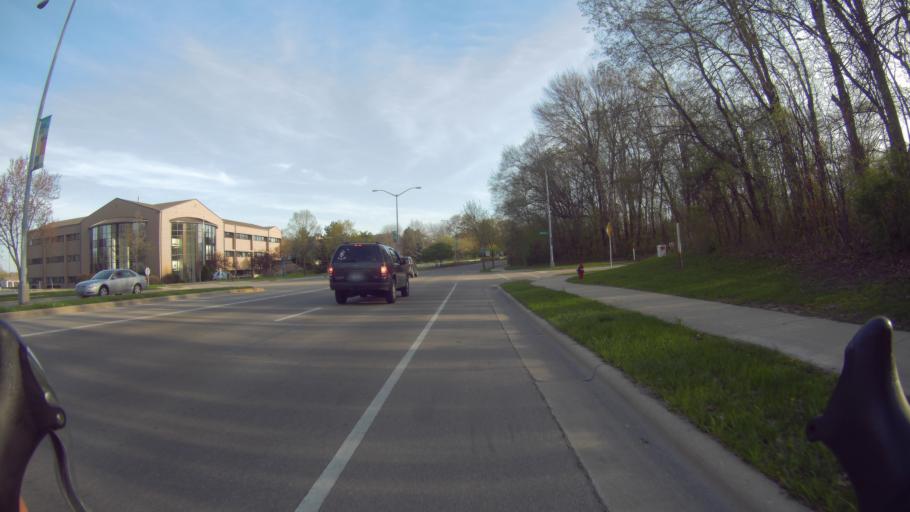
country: US
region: Wisconsin
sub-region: Dane County
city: Maple Bluff
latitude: 43.1257
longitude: -89.3501
